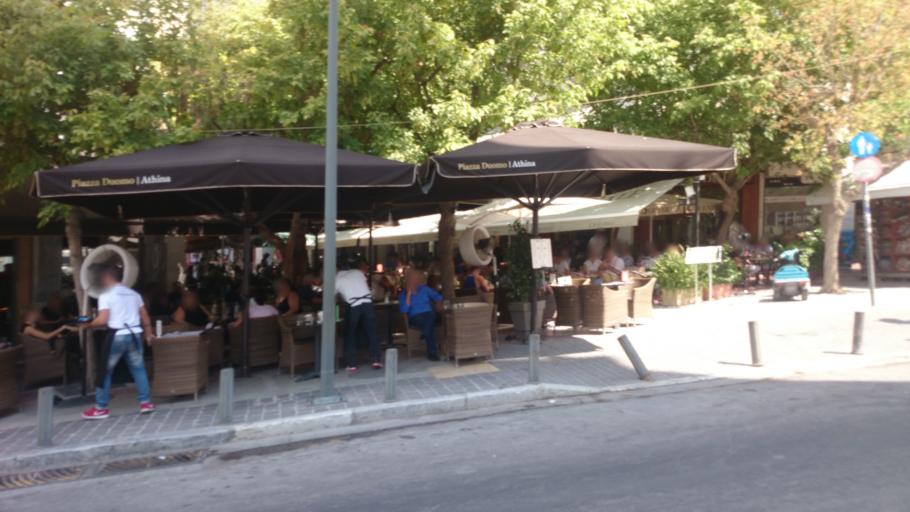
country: GR
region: Attica
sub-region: Nomarchia Athinas
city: Athens
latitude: 37.9755
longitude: 23.7298
